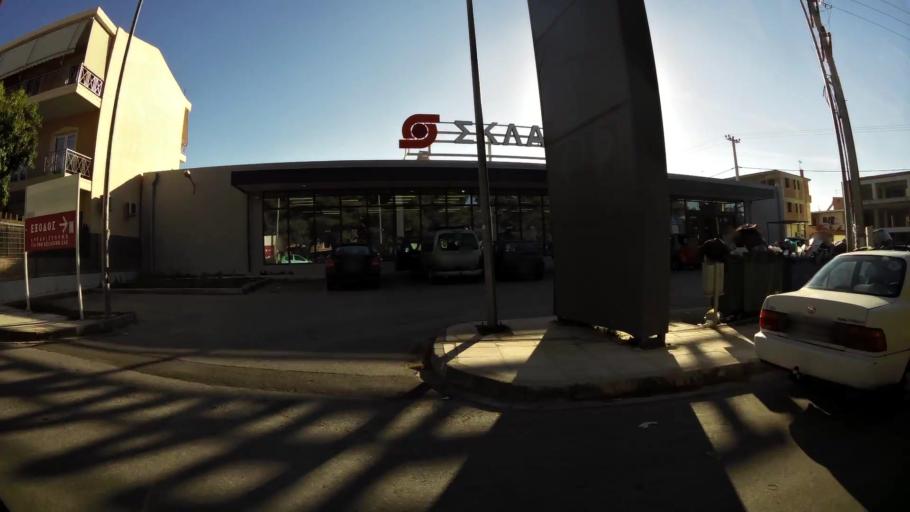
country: GR
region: Attica
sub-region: Nomarchia Anatolikis Attikis
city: Kalyvia Thorikou
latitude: 37.8441
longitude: 23.9273
